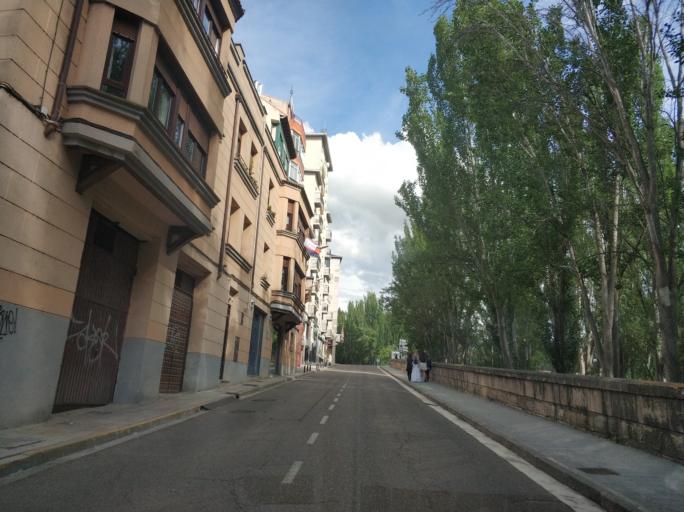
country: ES
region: Castille and Leon
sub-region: Provincia de Burgos
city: Aranda de Duero
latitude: 41.6707
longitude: -3.6908
